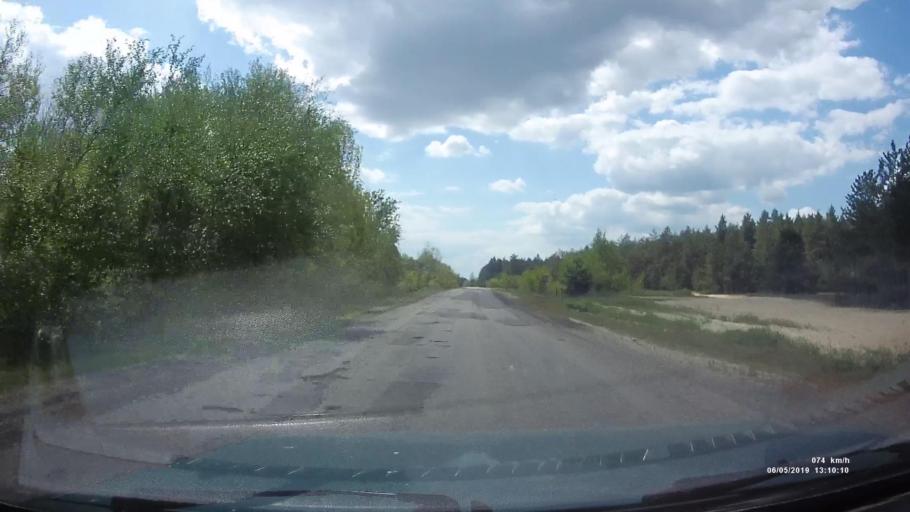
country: RU
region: Rostov
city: Ust'-Donetskiy
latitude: 47.7629
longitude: 40.9749
